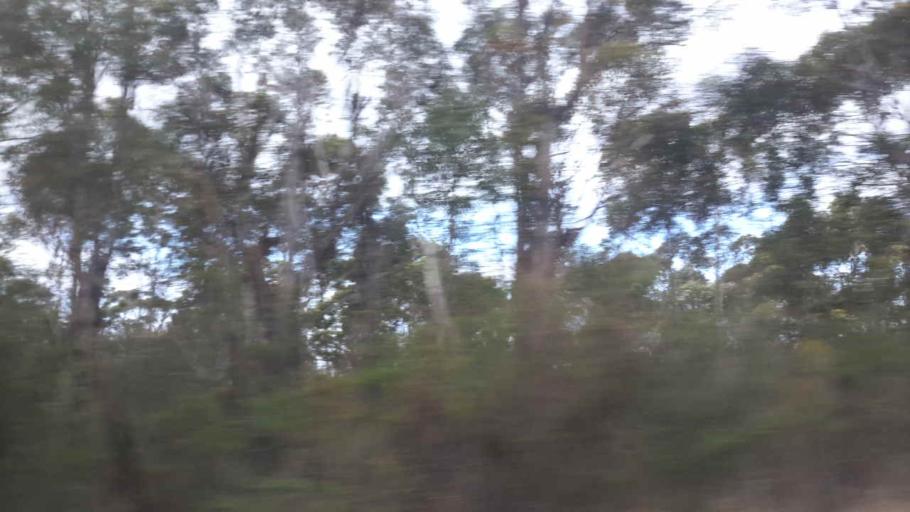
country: AU
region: New South Wales
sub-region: Wollondilly
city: Douglas Park
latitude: -34.2361
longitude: 150.8274
